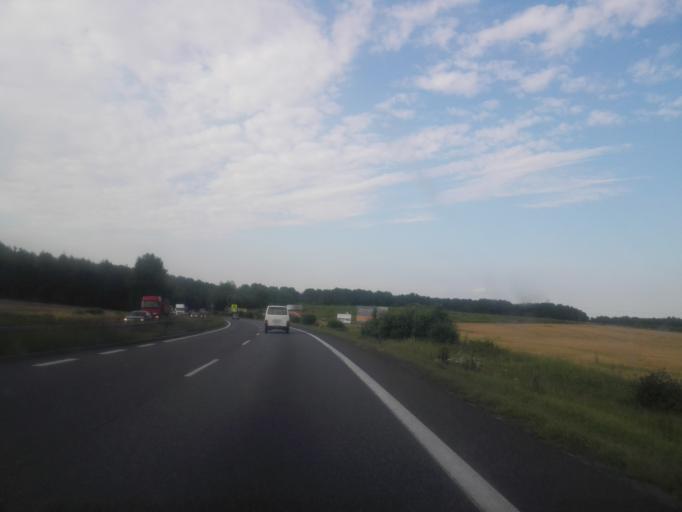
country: PL
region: Silesian Voivodeship
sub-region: Powiat bedzinski
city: Siewierz
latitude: 50.4441
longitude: 19.2226
